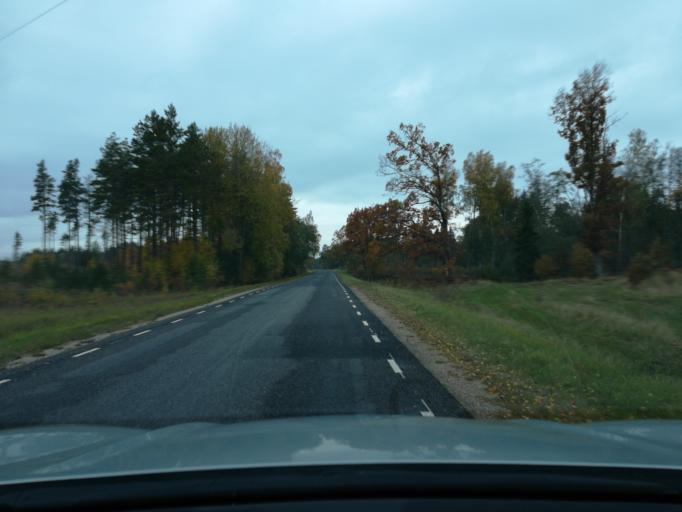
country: EE
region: Ida-Virumaa
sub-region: Johvi vald
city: Johvi
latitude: 59.0184
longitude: 27.4082
